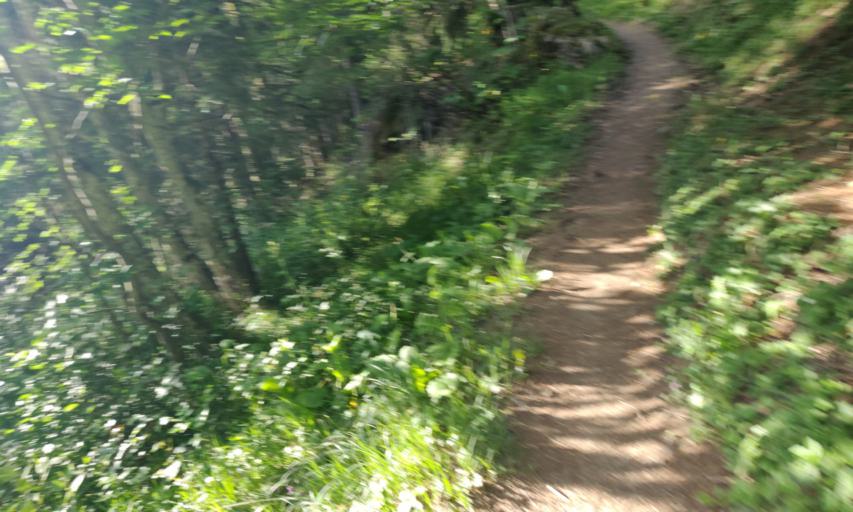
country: CH
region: Bern
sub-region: Obersimmental-Saanen District
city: Gstaad
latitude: 46.4079
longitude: 7.3398
